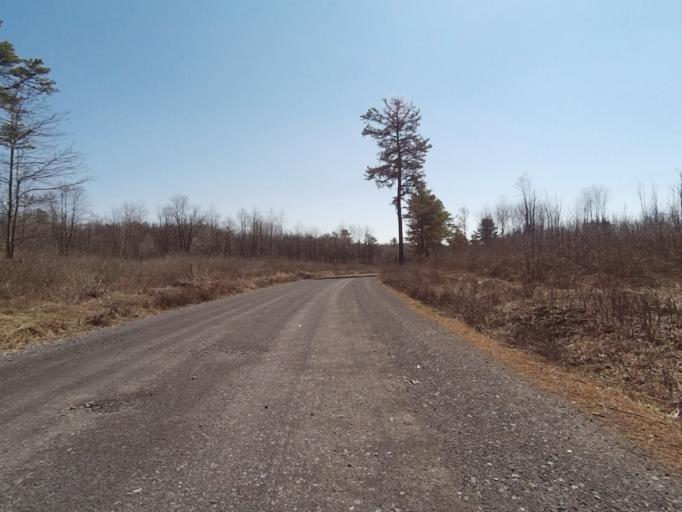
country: US
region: Pennsylvania
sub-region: Centre County
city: Park Forest Village
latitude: 40.7841
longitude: -77.9497
